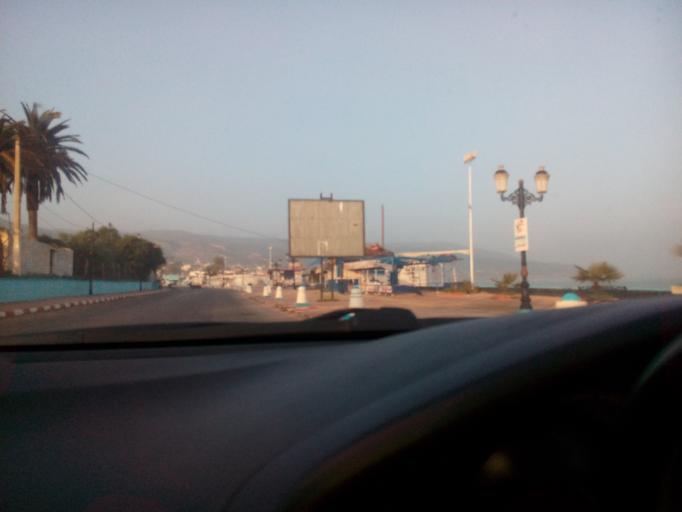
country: DZ
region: Oran
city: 'Ain el Turk
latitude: 35.7057
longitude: -0.8904
